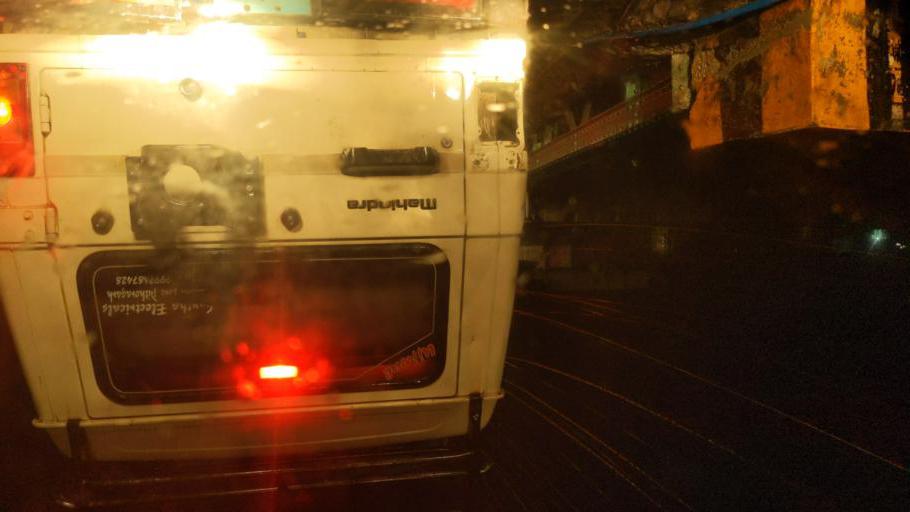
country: IN
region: Uttarakhand
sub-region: Naini Tal
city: Haldwani
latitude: 29.2709
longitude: 79.5441
